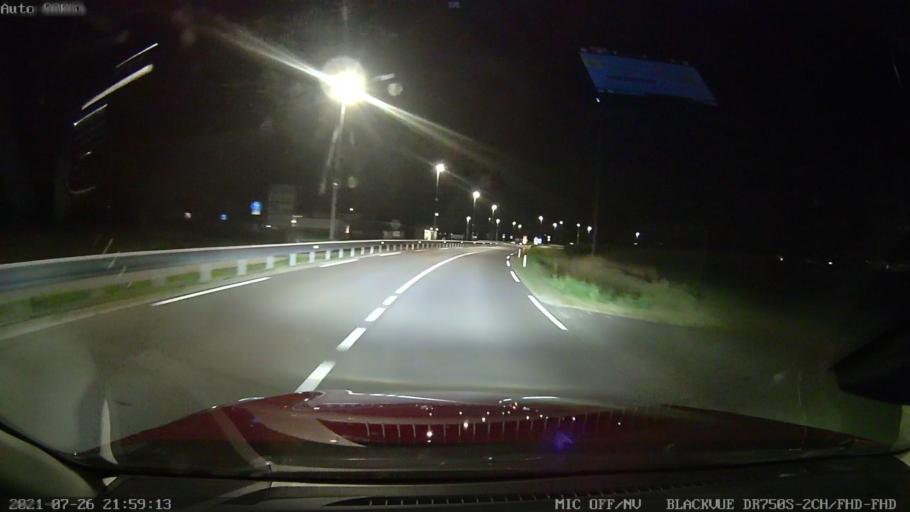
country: SI
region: Markovci
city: Markovci
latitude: 46.3977
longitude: 15.9338
